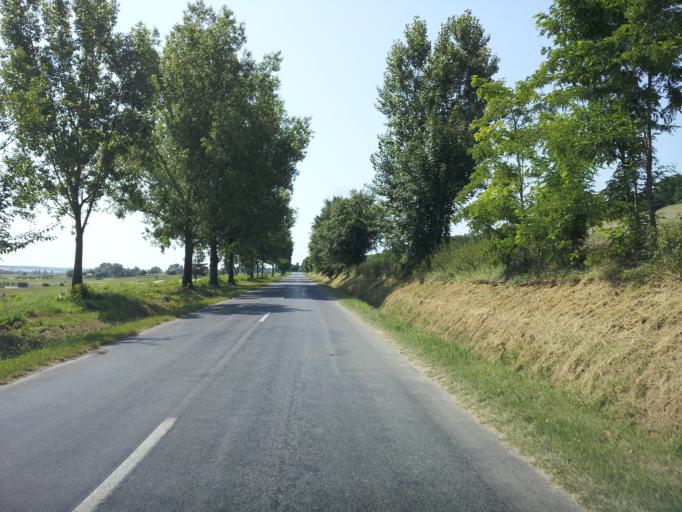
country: HU
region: Zala
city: Heviz
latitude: 46.8272
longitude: 17.0926
